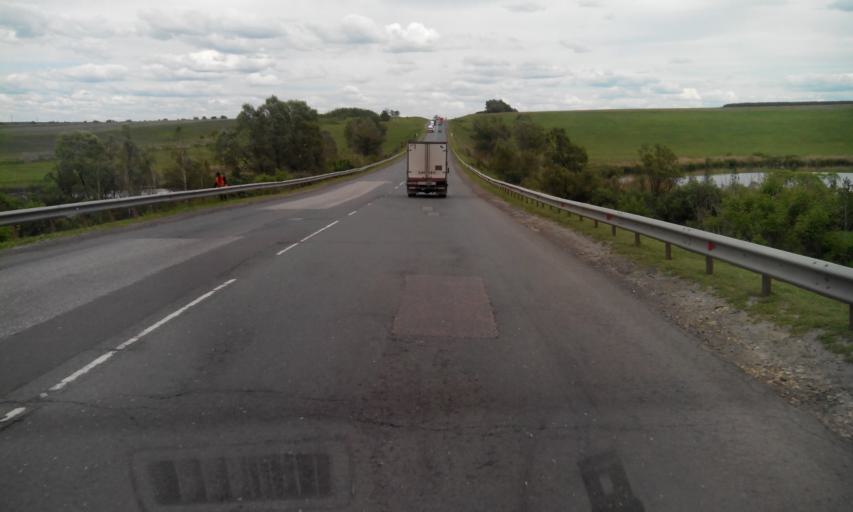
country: RU
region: Penza
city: Chemodanovka
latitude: 53.2302
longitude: 45.3620
